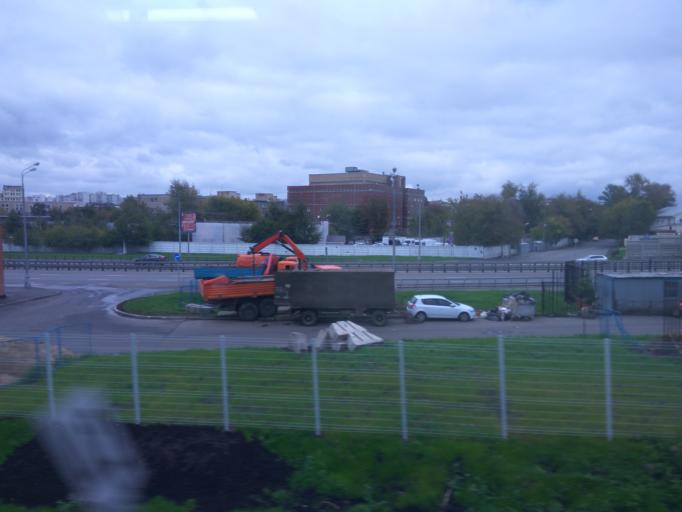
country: RU
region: Moskovskaya
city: Presnenskiy
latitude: 55.7647
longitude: 37.5190
